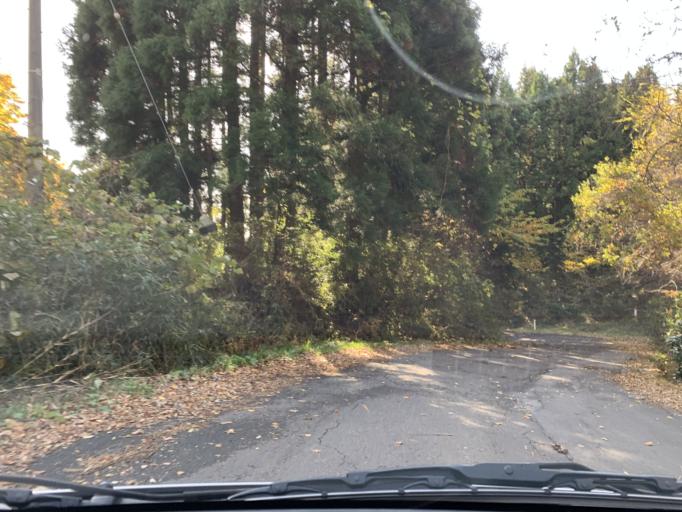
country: JP
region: Iwate
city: Ichinoseki
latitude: 39.0240
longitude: 141.0968
